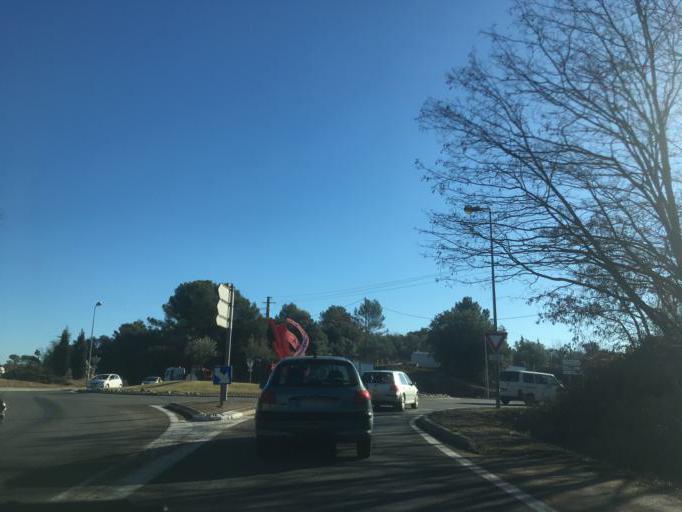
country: FR
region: Provence-Alpes-Cote d'Azur
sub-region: Departement du Var
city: Draguignan
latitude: 43.5269
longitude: 6.4366
